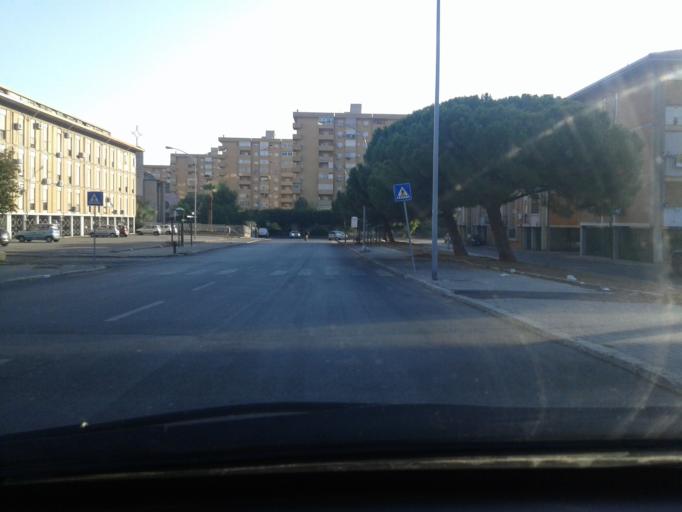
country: IT
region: Sicily
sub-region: Palermo
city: Palermo
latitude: 38.0900
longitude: 13.3581
